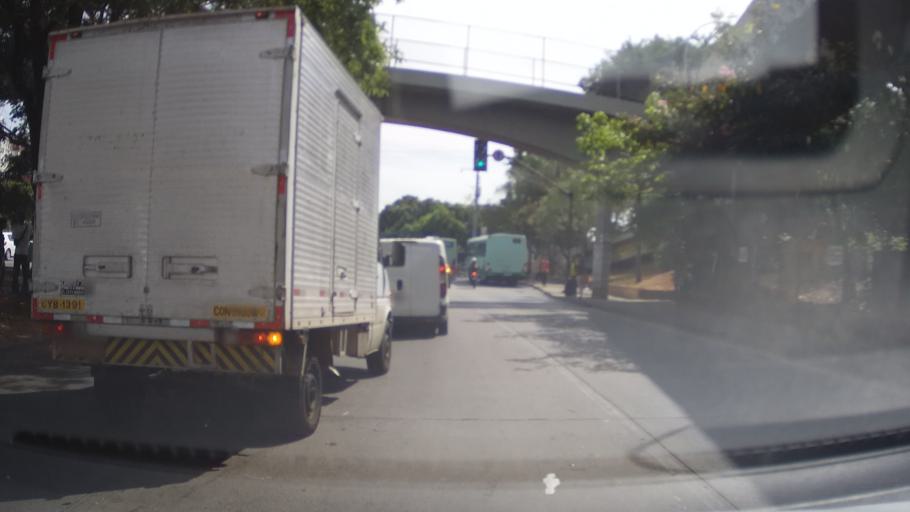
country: BR
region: Minas Gerais
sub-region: Belo Horizonte
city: Belo Horizonte
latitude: -19.9274
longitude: -43.9880
